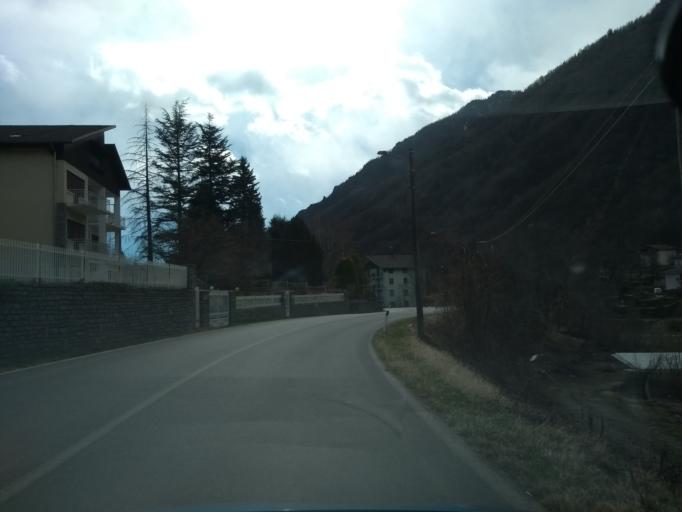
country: IT
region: Piedmont
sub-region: Provincia di Torino
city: Chialamberto
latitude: 45.3605
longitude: 7.3510
